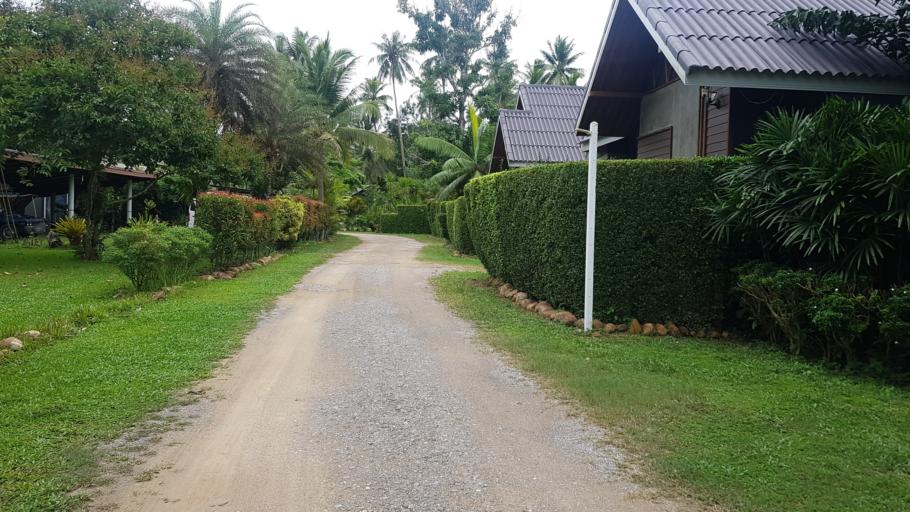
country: TH
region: Chumphon
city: Chumphon
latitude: 10.4692
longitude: 99.1934
